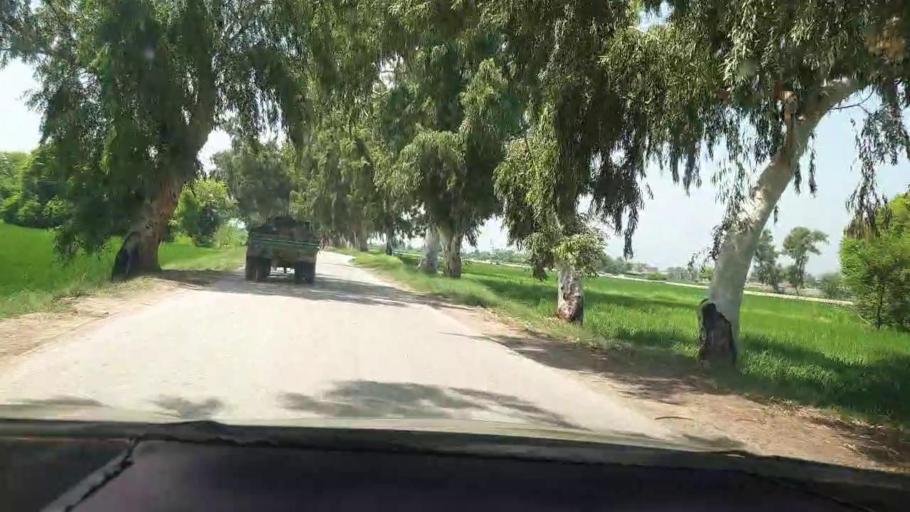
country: PK
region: Sindh
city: Kambar
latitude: 27.6092
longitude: 68.0443
